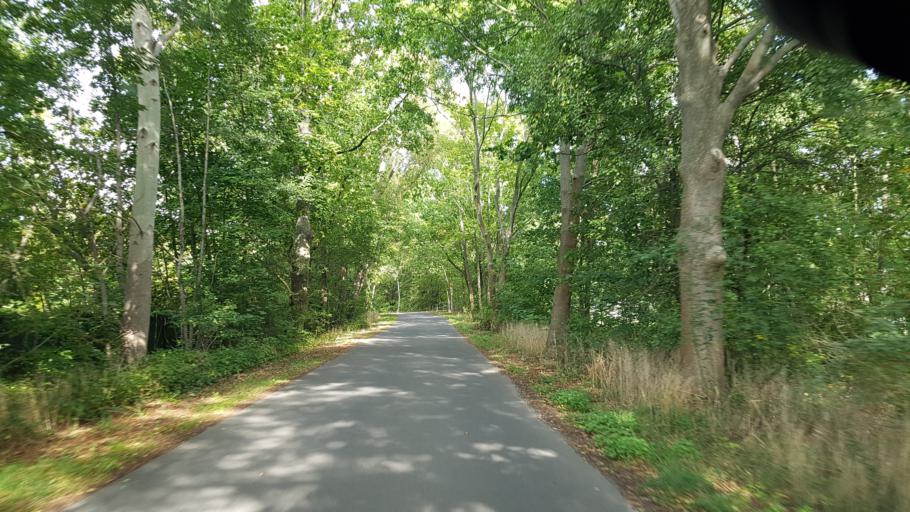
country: DE
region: Brandenburg
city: Doberlug-Kirchhain
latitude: 51.6087
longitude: 13.5416
